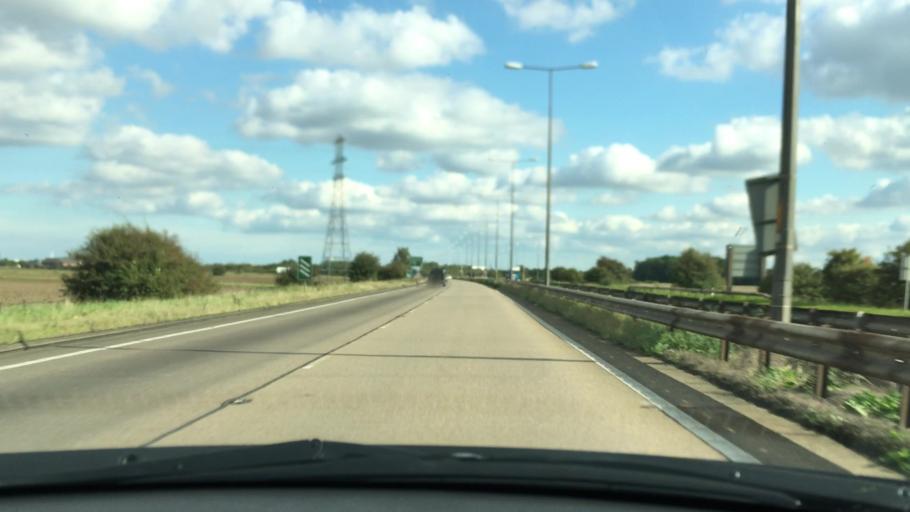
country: GB
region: England
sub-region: North East Lincolnshire
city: Healing
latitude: 53.5861
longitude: -0.1508
